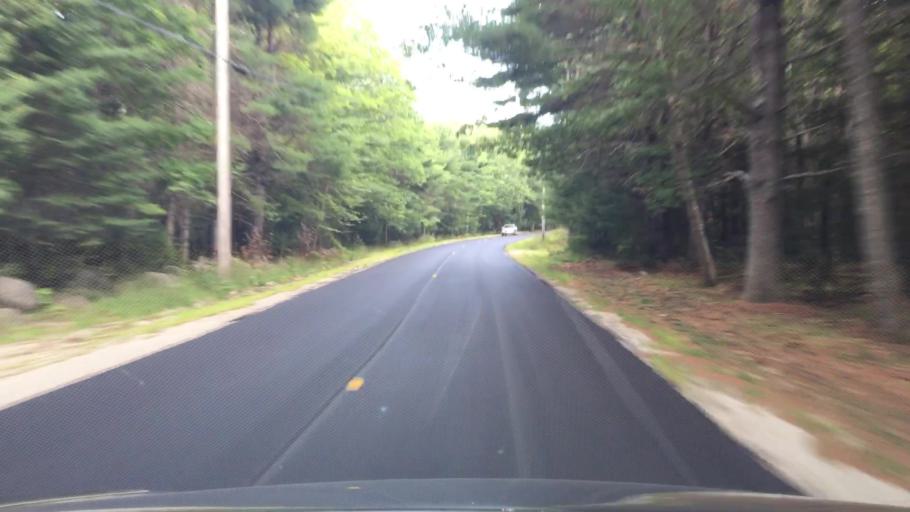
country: US
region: Maine
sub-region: Hancock County
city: Surry
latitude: 44.5232
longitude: -68.6088
